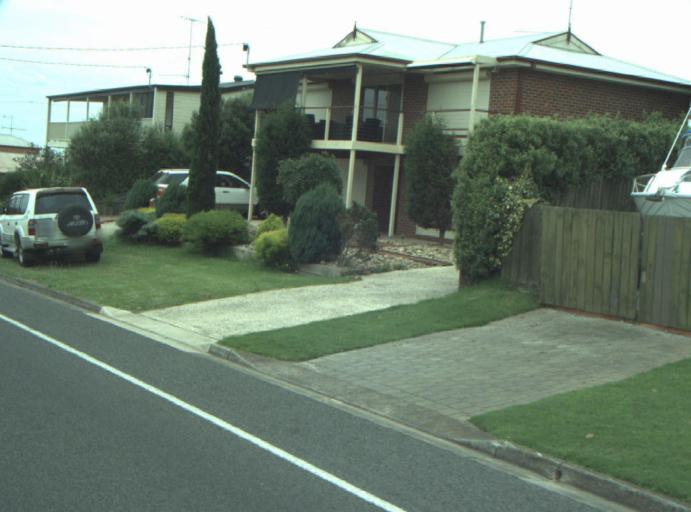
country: AU
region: Victoria
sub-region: Greater Geelong
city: Clifton Springs
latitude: -38.1480
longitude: 144.5756
